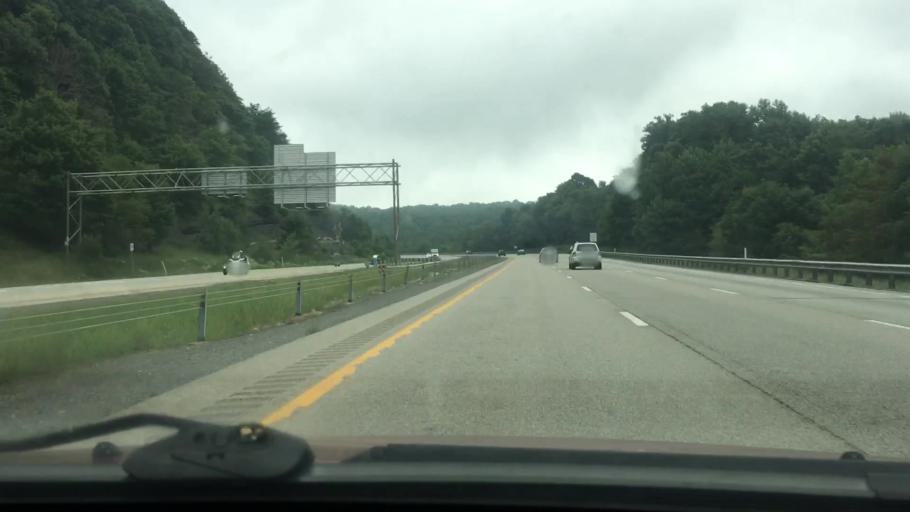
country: US
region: West Virginia
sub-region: Monongalia County
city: Cheat Lake
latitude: 39.6583
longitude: -79.8369
